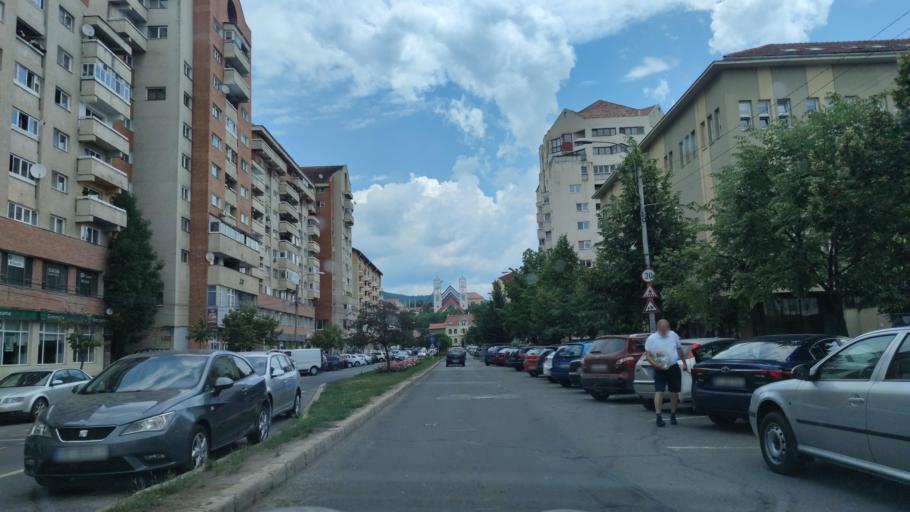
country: RO
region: Harghita
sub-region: Municipiul Miercurea Ciuc
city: Miercurea-Ciuc
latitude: 46.3621
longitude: 25.8025
